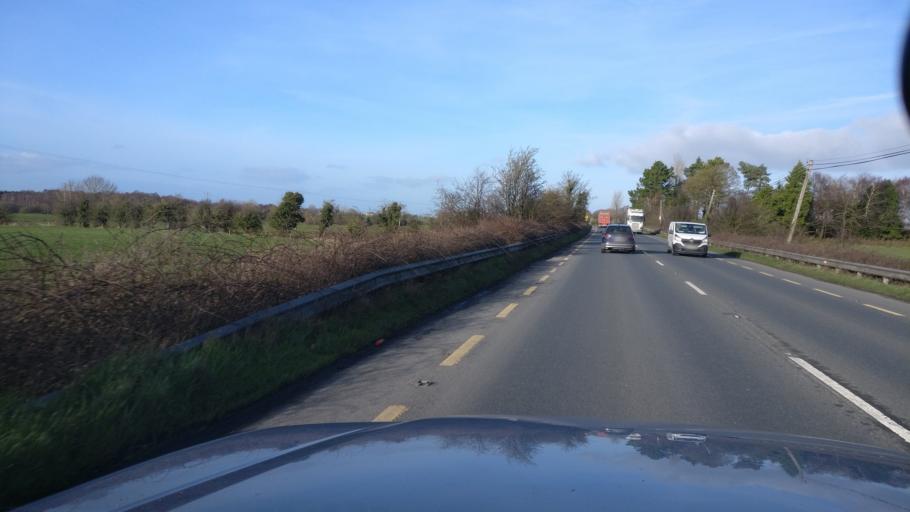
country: IE
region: Leinster
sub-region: Uibh Fhaili
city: Tullamore
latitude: 53.2435
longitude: -7.4778
